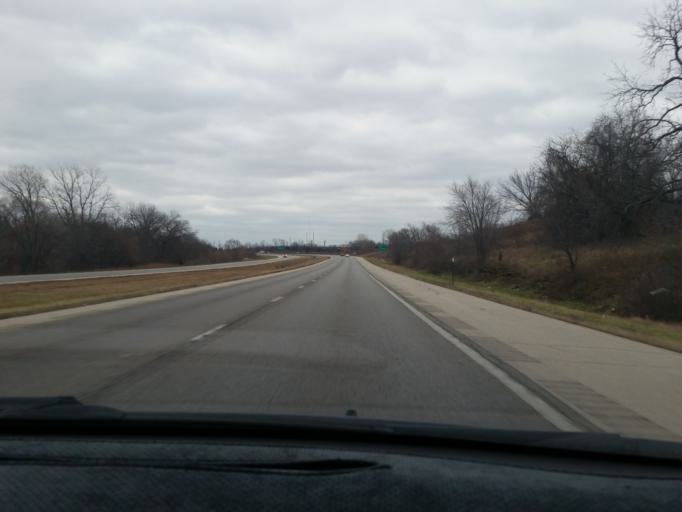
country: US
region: Kansas
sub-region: Johnson County
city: Olathe
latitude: 38.9436
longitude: -94.8726
